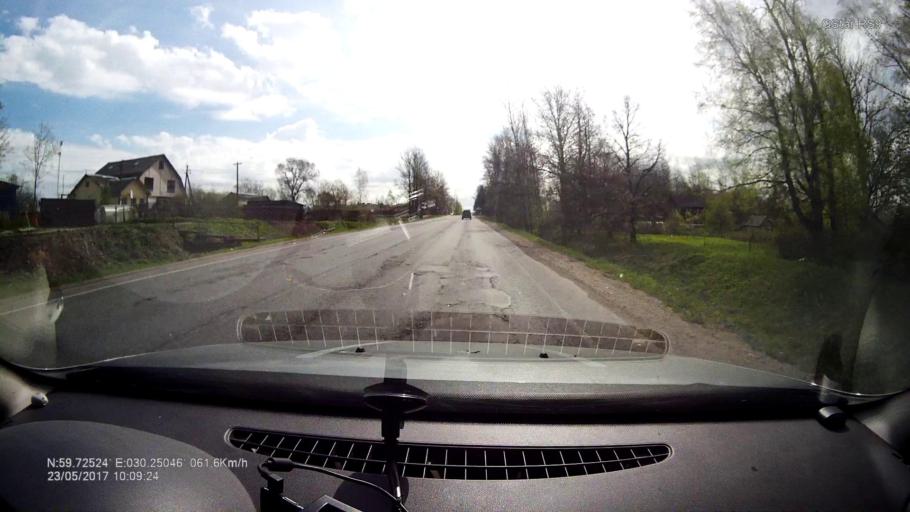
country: RU
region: St.-Petersburg
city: Aleksandrovskaya
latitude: 59.7252
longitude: 30.2507
